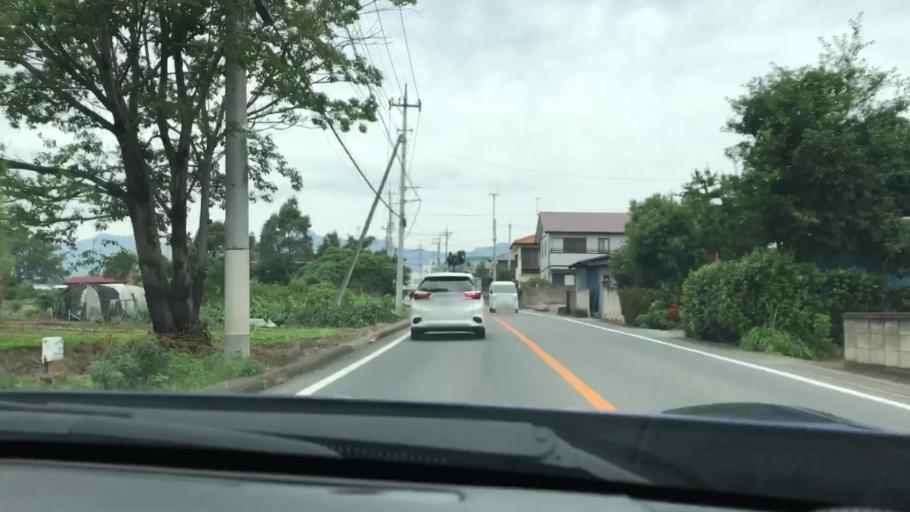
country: JP
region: Gunma
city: Kanekomachi
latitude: 36.3979
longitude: 138.9923
